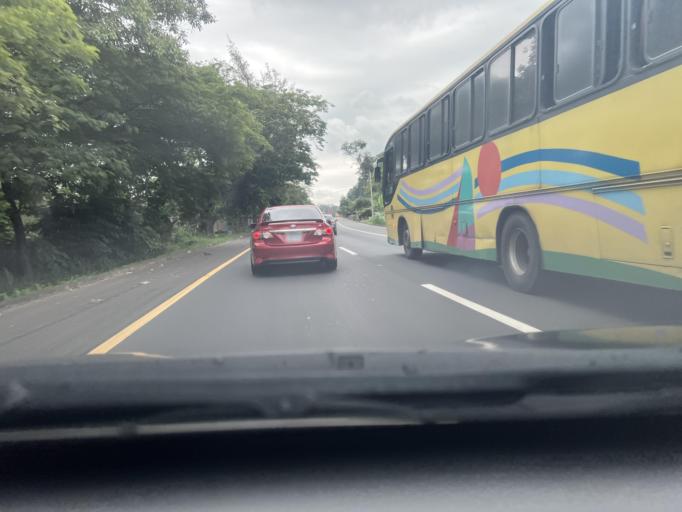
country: SV
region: Santa Ana
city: El Congo
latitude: 13.8805
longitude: -89.4919
